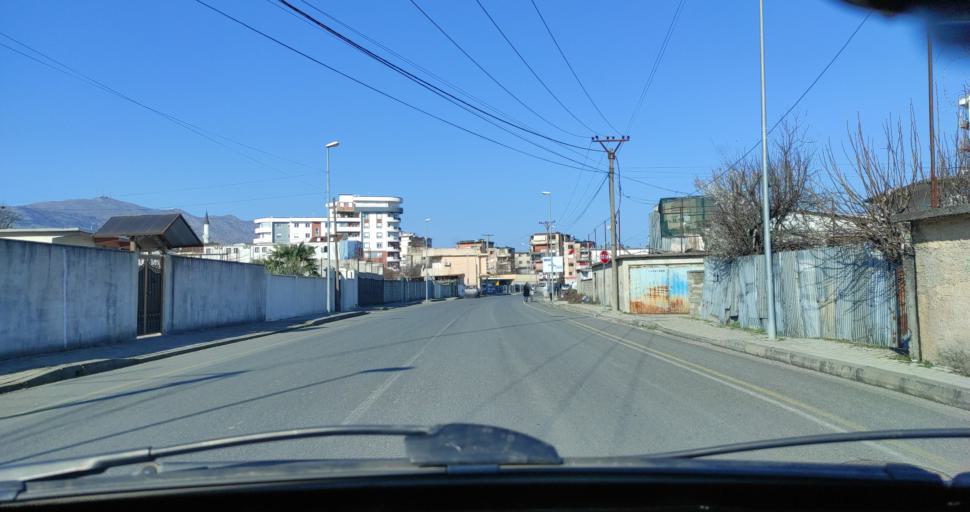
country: AL
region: Shkoder
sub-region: Rrethi i Shkodres
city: Shkoder
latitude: 42.0572
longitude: 19.5059
